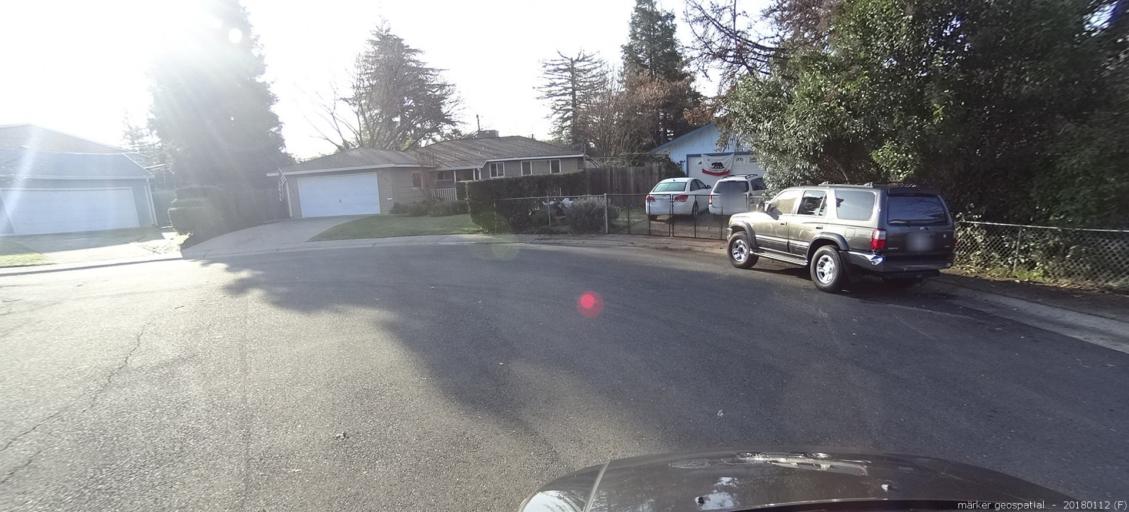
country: US
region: California
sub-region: Sacramento County
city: Fair Oaks
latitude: 38.6145
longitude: -121.2814
